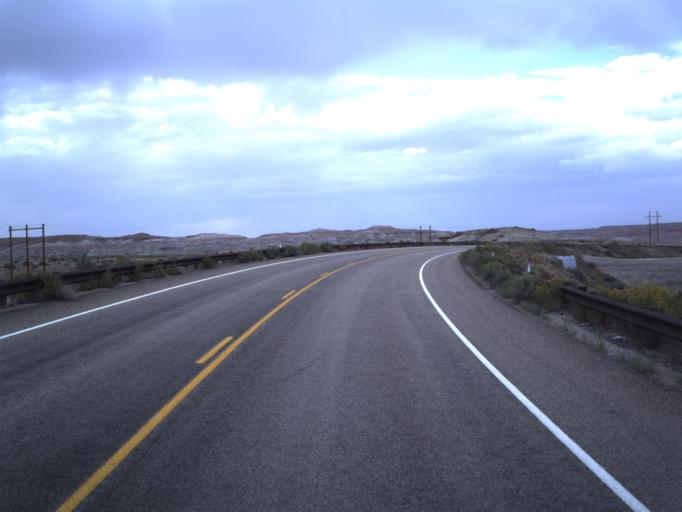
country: US
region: Colorado
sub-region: Rio Blanco County
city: Rangely
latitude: 40.0945
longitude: -109.2265
